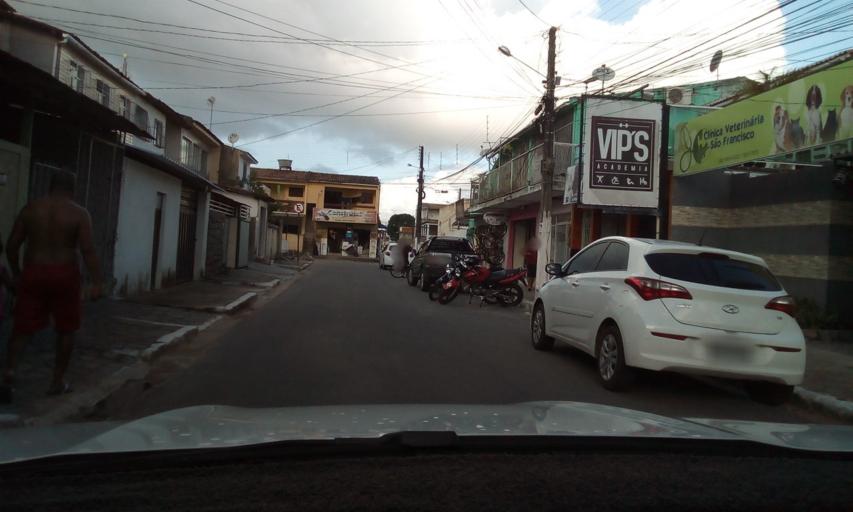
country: BR
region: Paraiba
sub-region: Joao Pessoa
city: Joao Pessoa
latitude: -7.1667
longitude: -34.8371
